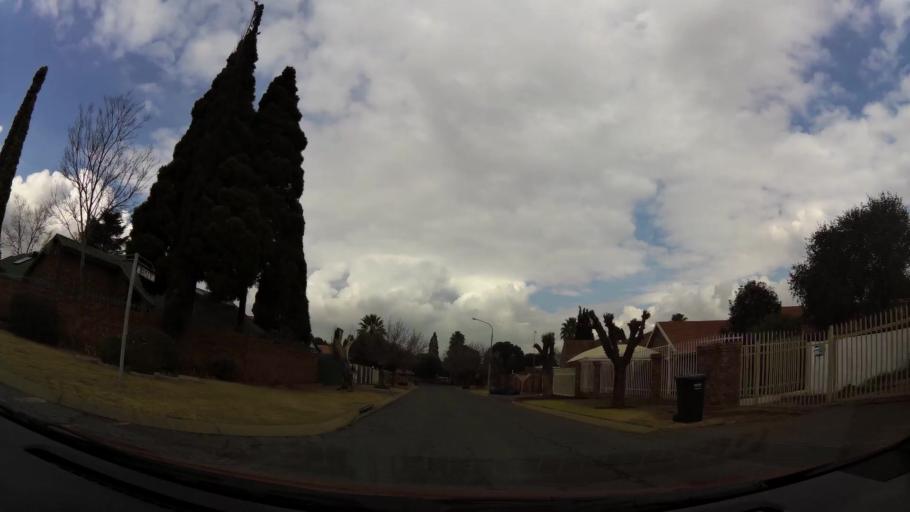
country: ZA
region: Gauteng
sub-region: Sedibeng District Municipality
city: Vanderbijlpark
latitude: -26.7350
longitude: 27.8501
